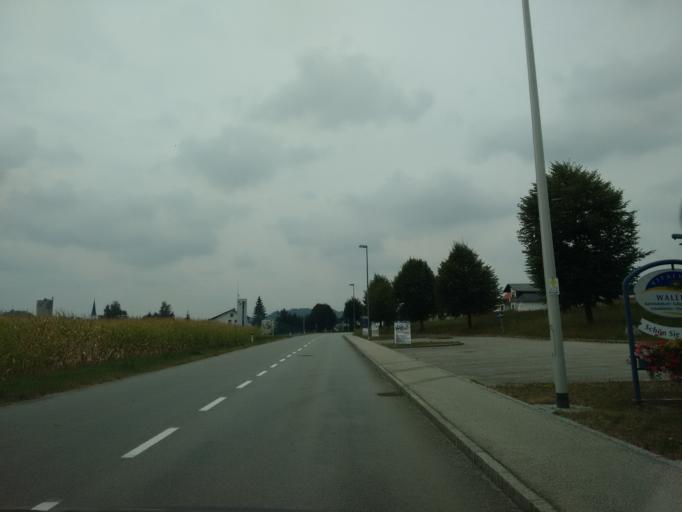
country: AT
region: Upper Austria
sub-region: Politischer Bezirk Grieskirchen
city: Bad Schallerbach
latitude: 48.2355
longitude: 13.9512
